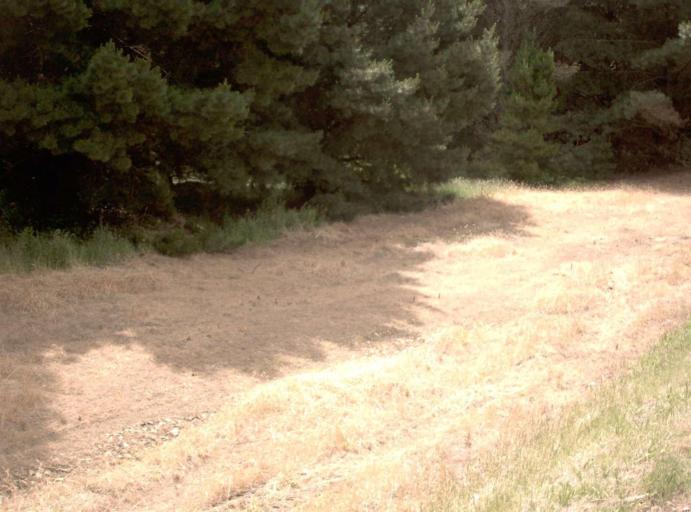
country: AU
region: Victoria
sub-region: Latrobe
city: Traralgon
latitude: -38.3839
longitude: 146.6649
